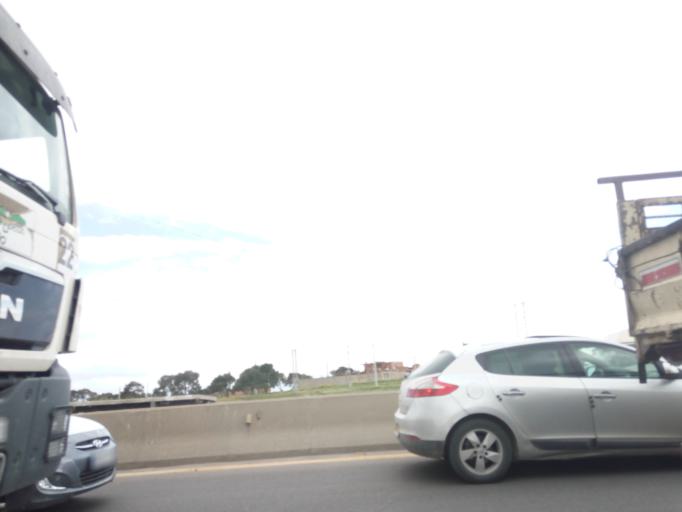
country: DZ
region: Bordj Bou Arreridj
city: Bordj Bou Arreridj
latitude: 36.0961
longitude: 4.7585
